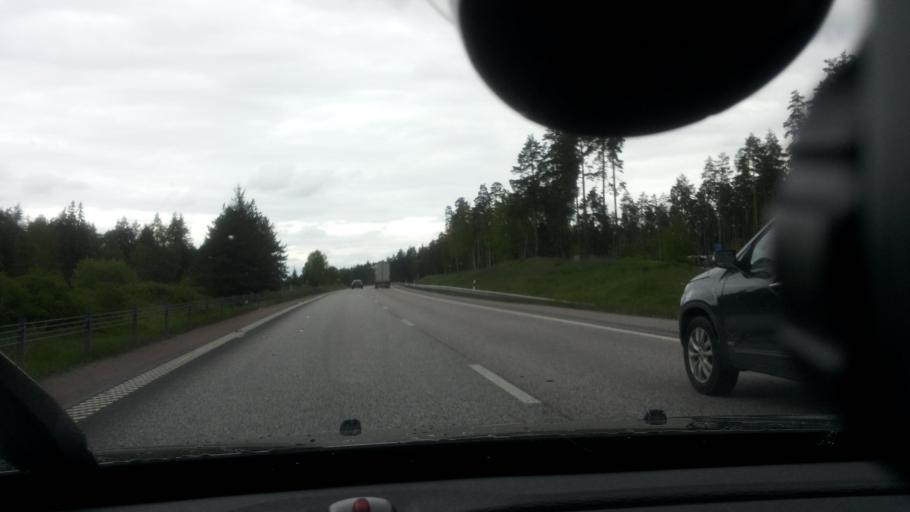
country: SE
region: Uppsala
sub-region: Uppsala Kommun
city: Alsike
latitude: 59.7912
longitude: 17.7748
